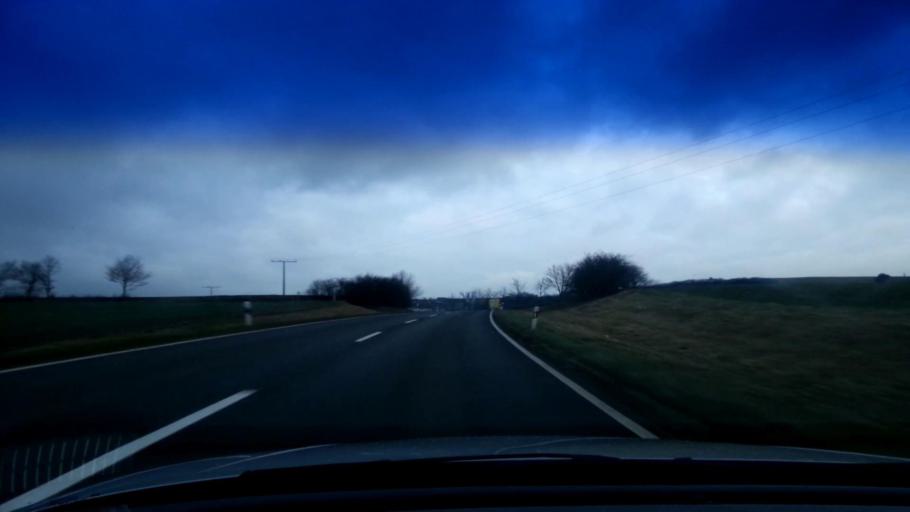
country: DE
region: Bavaria
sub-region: Upper Franconia
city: Burgebrach
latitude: 49.8546
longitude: 10.7256
